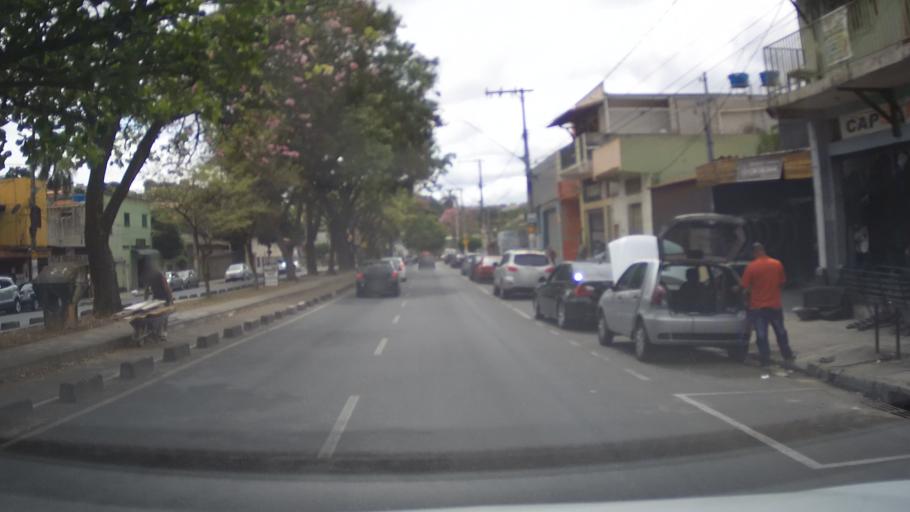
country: BR
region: Minas Gerais
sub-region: Belo Horizonte
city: Belo Horizonte
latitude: -19.8407
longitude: -43.9263
